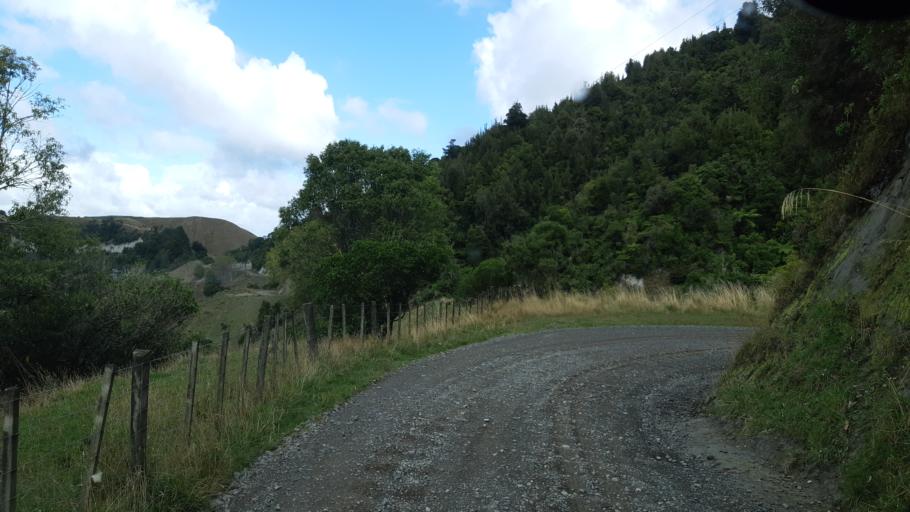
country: NZ
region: Manawatu-Wanganui
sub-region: Ruapehu District
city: Waiouru
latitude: -39.7940
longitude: 175.6755
